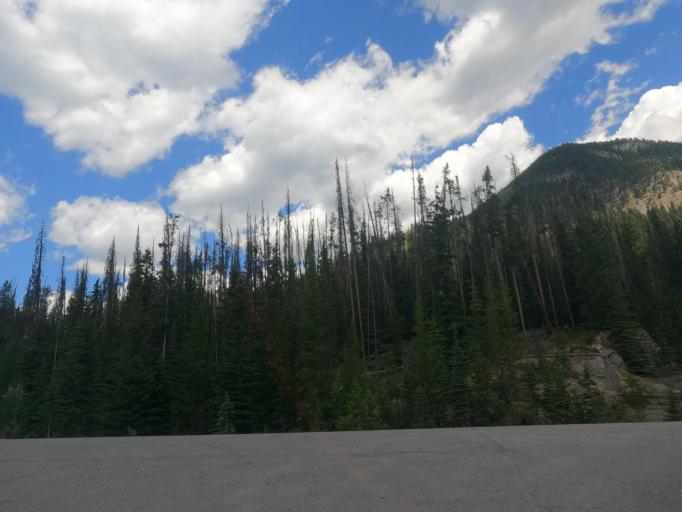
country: CA
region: Alberta
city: Lake Louise
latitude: 51.3826
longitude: -116.5308
